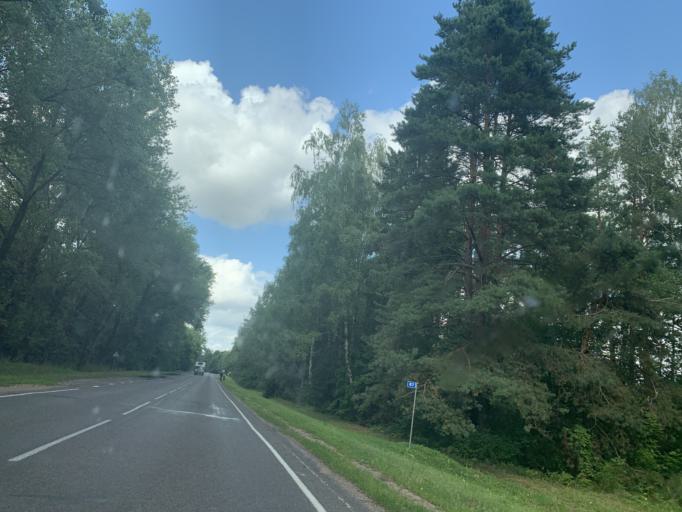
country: BY
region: Minsk
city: Enyerhyetykaw
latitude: 53.5654
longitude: 27.0620
